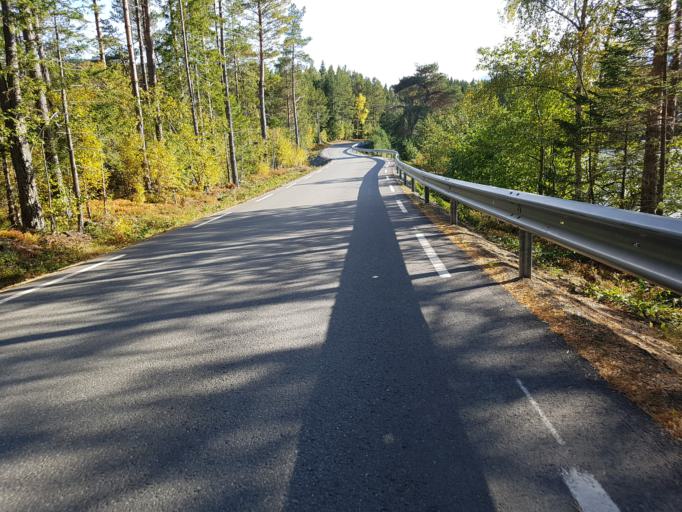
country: NO
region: Sor-Trondelag
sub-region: Malvik
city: Malvik
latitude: 63.3815
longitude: 10.5984
